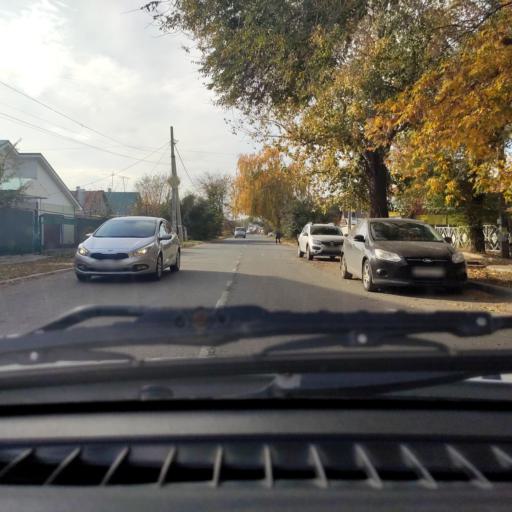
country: RU
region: Samara
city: Tol'yatti
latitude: 53.5277
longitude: 49.4118
